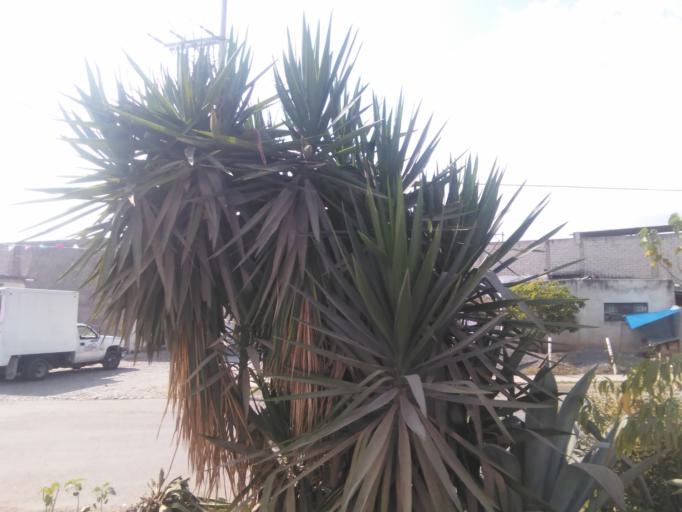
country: MX
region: Nayarit
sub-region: Tepic
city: La Corregidora
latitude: 21.4837
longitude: -104.8335
